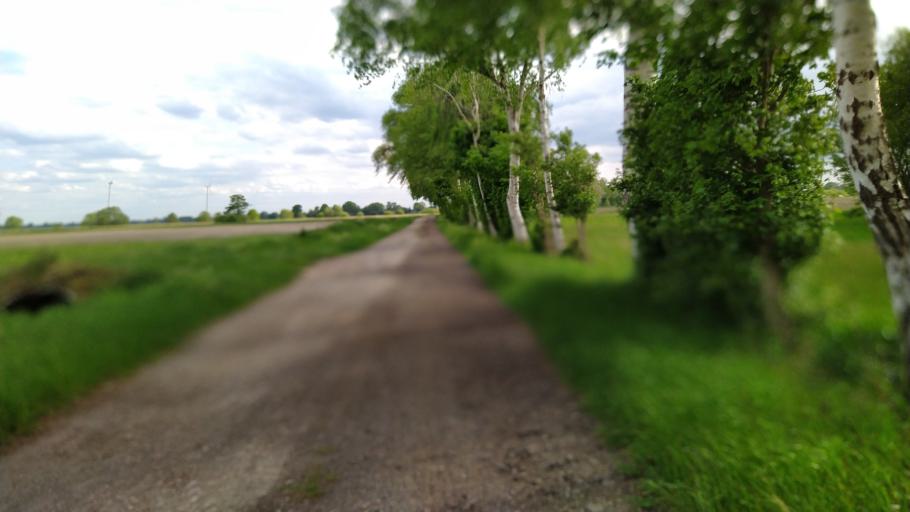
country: DE
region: Lower Saxony
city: Grasberg
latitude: 53.1986
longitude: 9.0292
